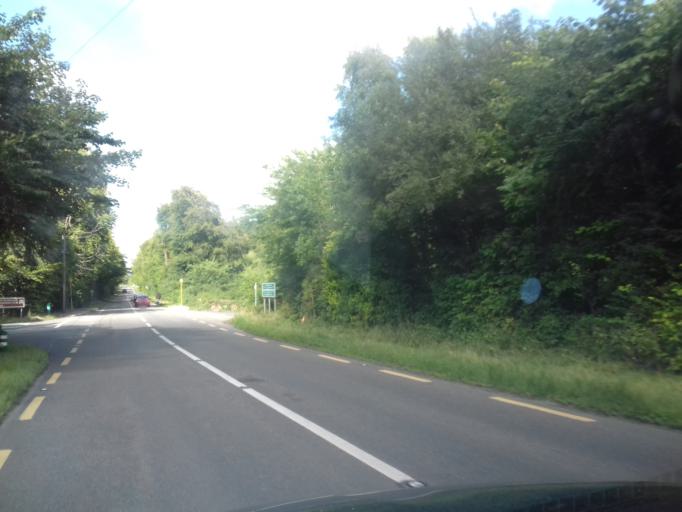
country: IE
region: Leinster
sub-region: Wicklow
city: Valleymount
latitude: 53.1403
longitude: -6.5609
